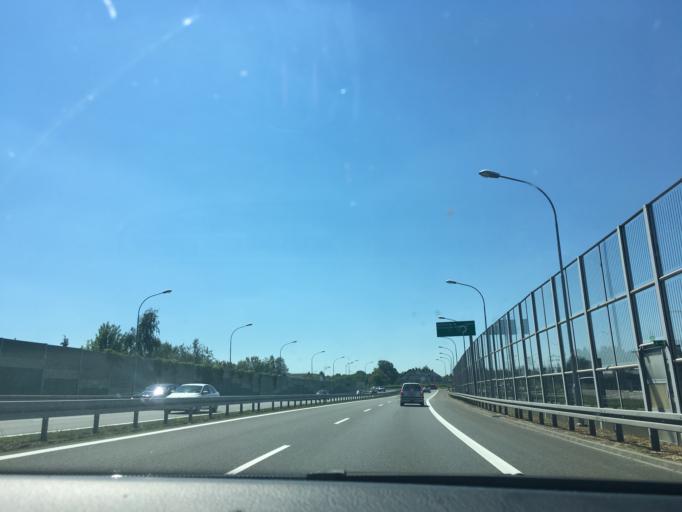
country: PL
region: Subcarpathian Voivodeship
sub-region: Powiat rzeszowski
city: Trzebownisko
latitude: 50.0571
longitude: 22.0394
